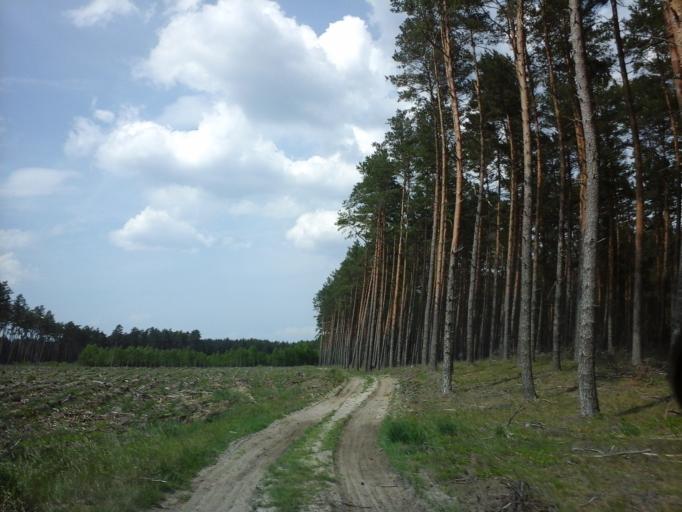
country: PL
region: West Pomeranian Voivodeship
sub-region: Powiat choszczenski
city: Drawno
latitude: 53.1378
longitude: 15.7887
